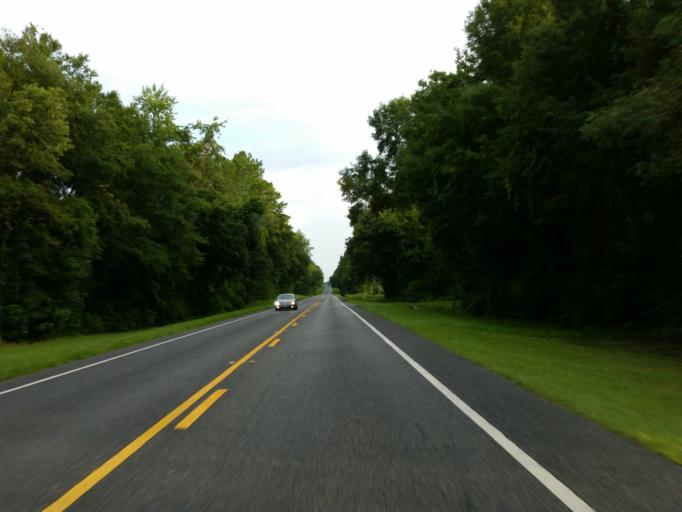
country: US
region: Florida
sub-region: Alachua County
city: High Springs
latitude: 29.9294
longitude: -82.6093
